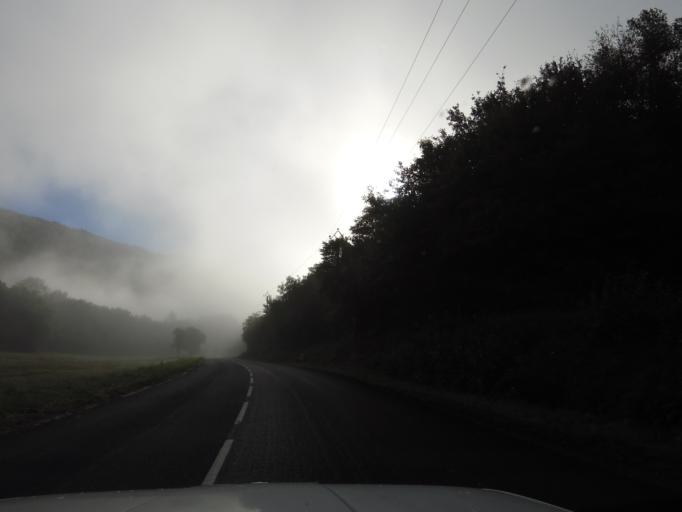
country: FR
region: Rhone-Alpes
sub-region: Departement de l'Isere
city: Creys-Mepieu
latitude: 45.7598
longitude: 5.4919
